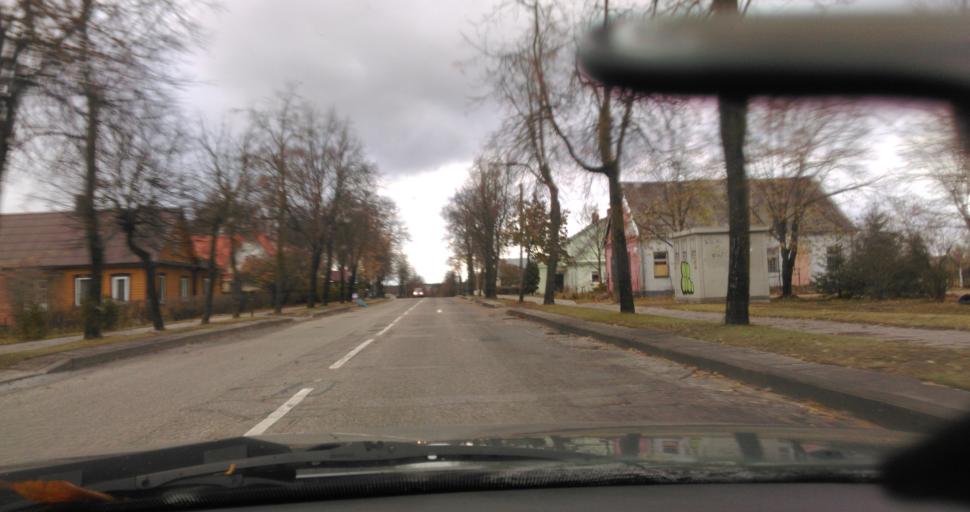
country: LT
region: Utenos apskritis
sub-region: Utena
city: Utena
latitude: 55.5016
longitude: 25.6095
